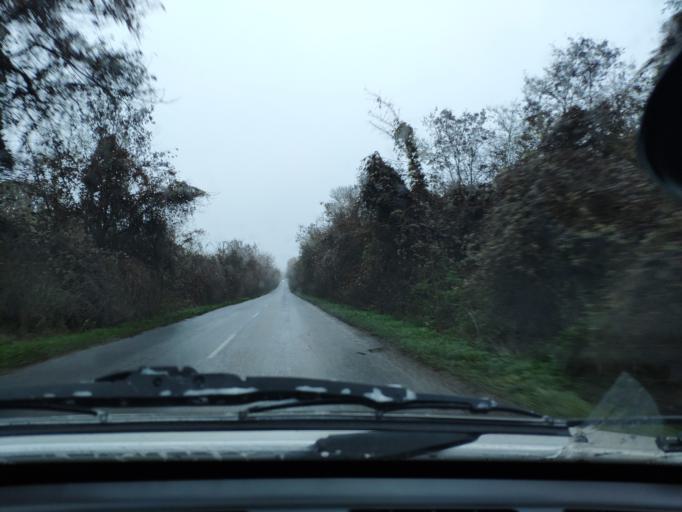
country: HU
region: Pest
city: Paty
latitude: 47.5303
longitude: 18.8386
